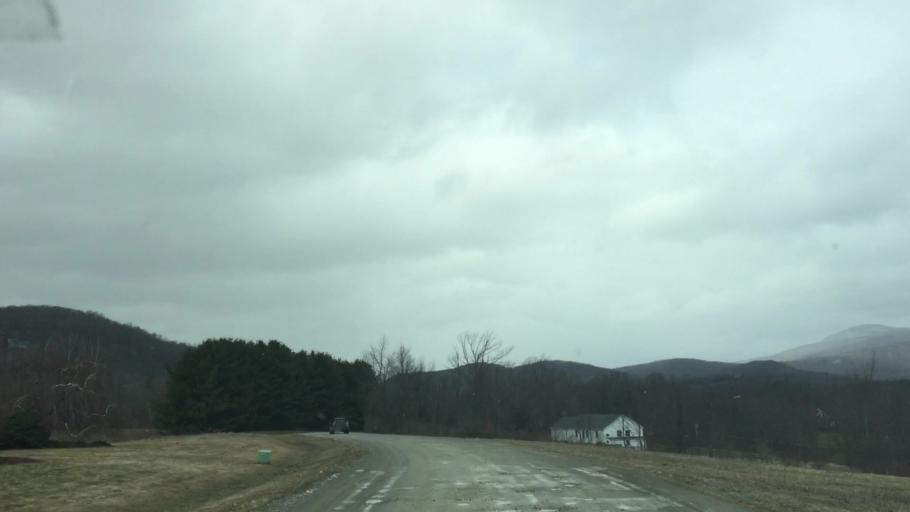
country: US
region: Massachusetts
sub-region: Berkshire County
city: Lanesborough
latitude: 42.5440
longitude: -73.2422
